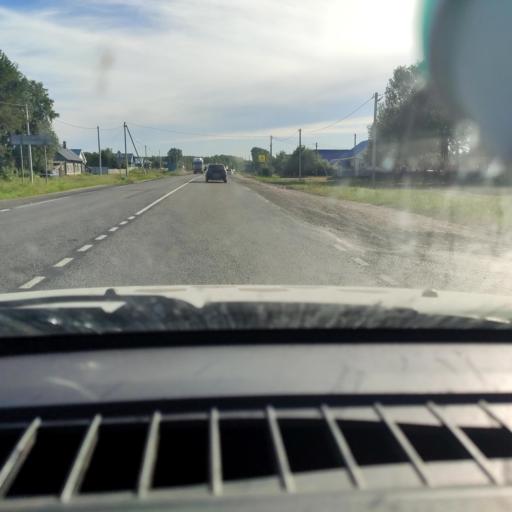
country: RU
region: Kirov
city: Vakhrushi
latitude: 58.6720
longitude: 49.9440
